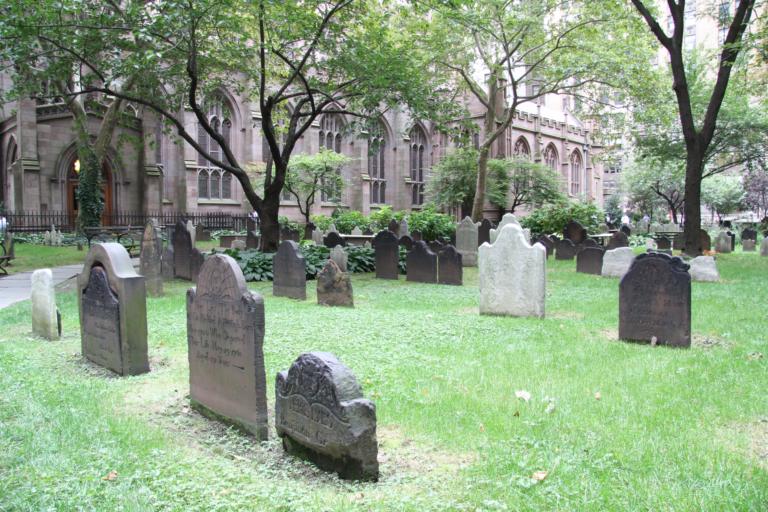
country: US
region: New York
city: New York City
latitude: 40.7082
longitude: -74.0118
